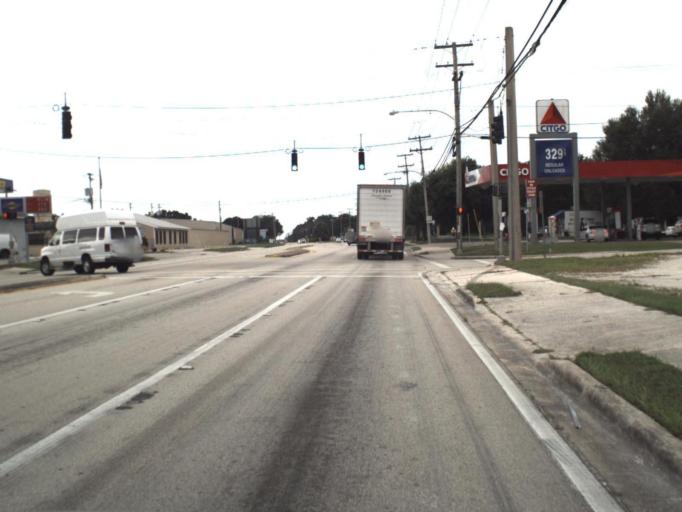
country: US
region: Florida
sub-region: Polk County
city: Bartow
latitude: 27.8828
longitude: -81.8285
